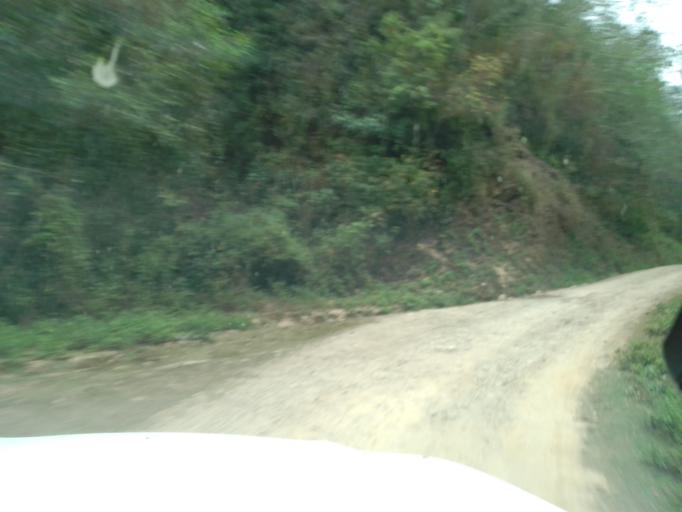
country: MX
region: Chiapas
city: Motozintla de Mendoza
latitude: 15.2177
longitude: -92.2226
